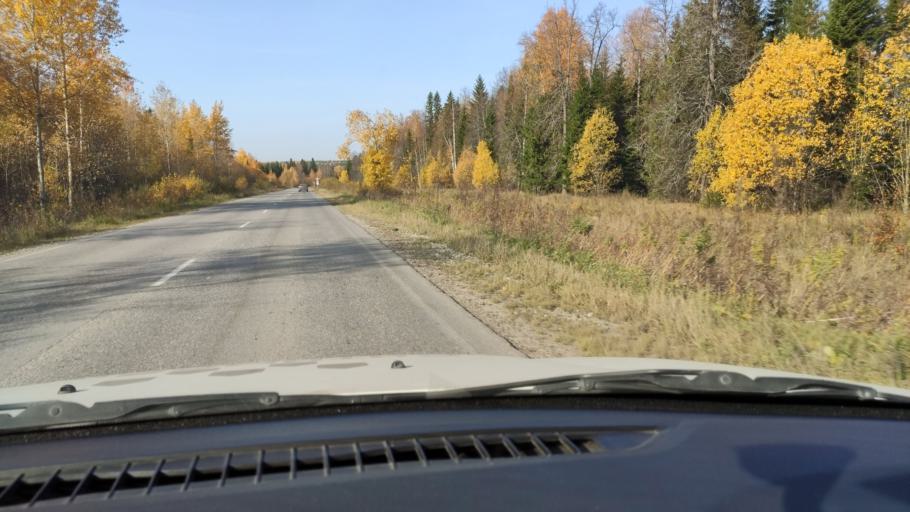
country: RU
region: Perm
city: Novyye Lyady
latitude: 58.0364
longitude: 56.6019
